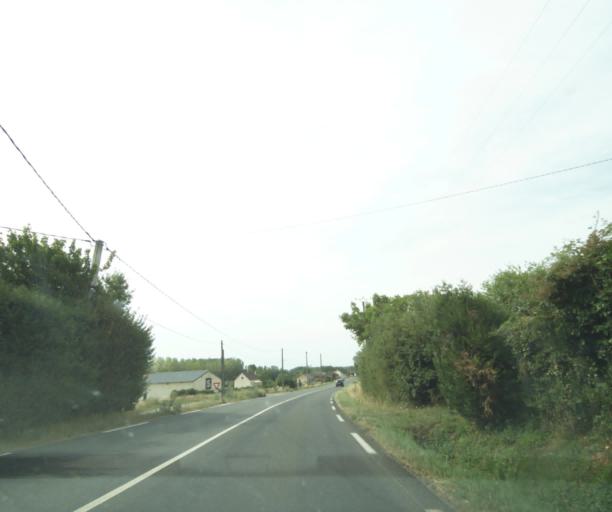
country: FR
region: Centre
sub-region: Departement d'Indre-et-Loire
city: Saint-Christophe-sur-le-Nais
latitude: 47.6592
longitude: 0.4778
